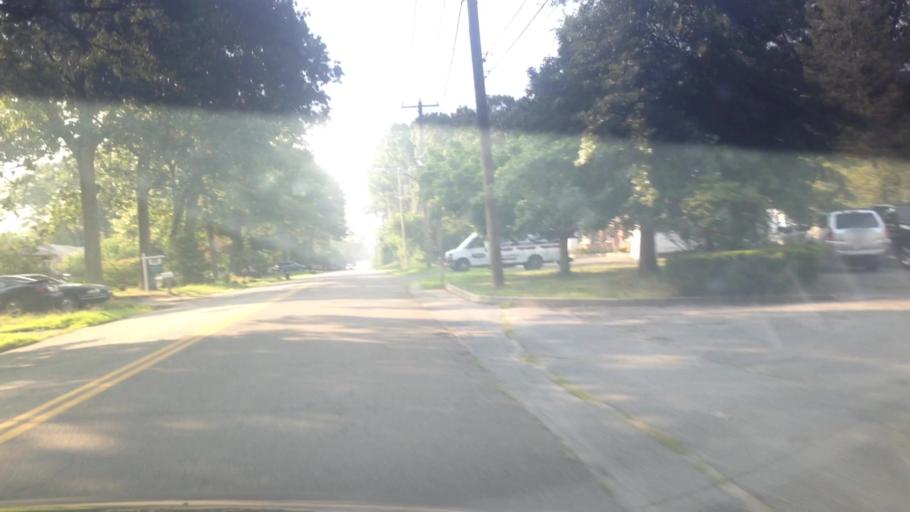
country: US
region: New York
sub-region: Suffolk County
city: Riverhead
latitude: 40.9263
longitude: -72.6824
